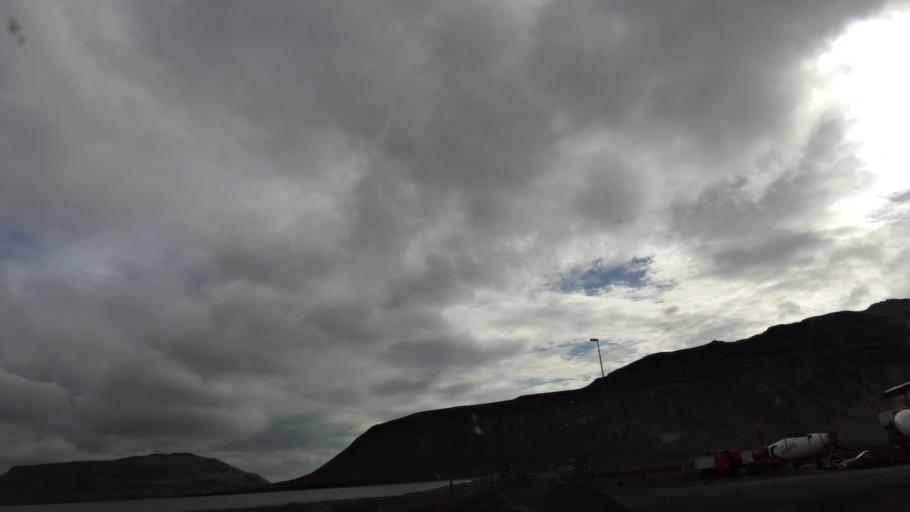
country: IS
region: West
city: Olafsvik
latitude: 64.9216
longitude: -23.2373
